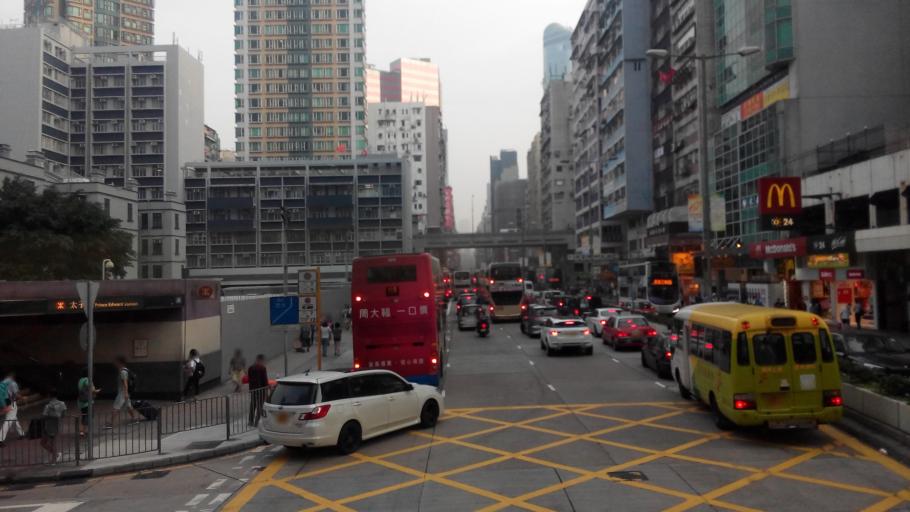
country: HK
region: Sham Shui Po
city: Sham Shui Po
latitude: 22.3251
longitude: 114.1683
